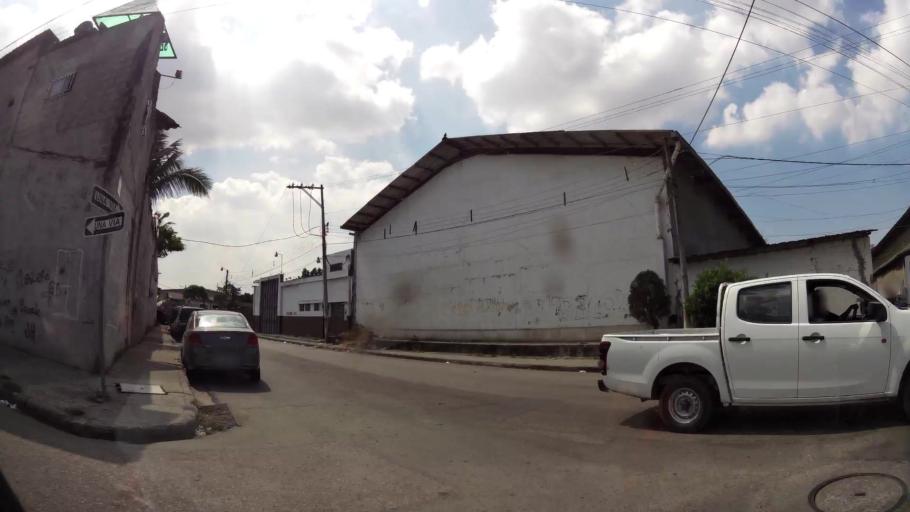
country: EC
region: Guayas
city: Guayaquil
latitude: -2.1341
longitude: -79.9364
